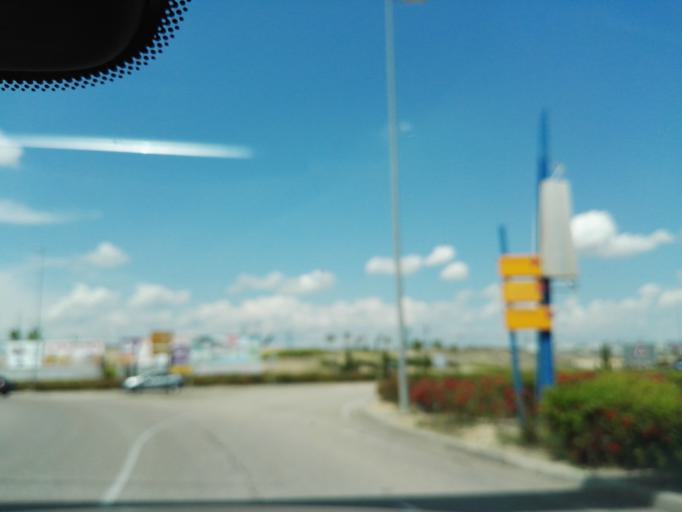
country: ES
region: Aragon
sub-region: Provincia de Zaragoza
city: Montecanal
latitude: 41.6331
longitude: -0.9880
